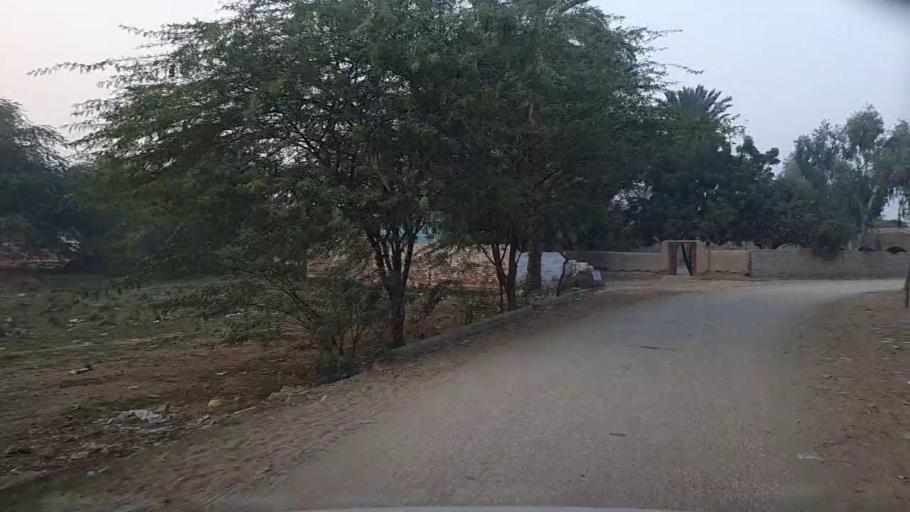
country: PK
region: Sindh
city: Bozdar
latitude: 27.0711
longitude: 68.5981
